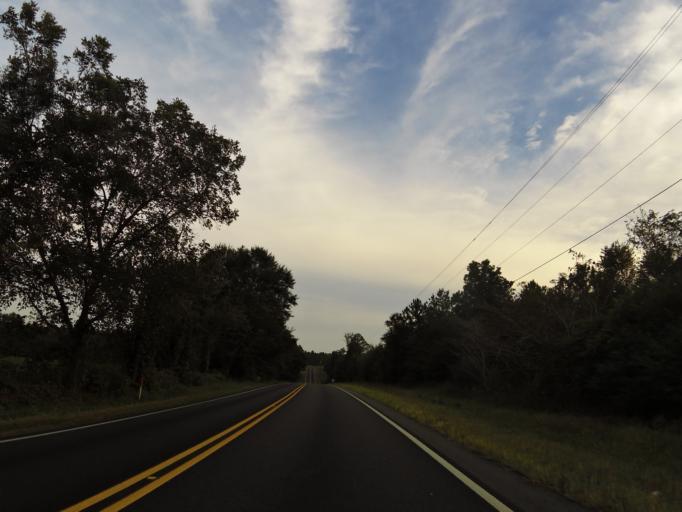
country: US
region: Alabama
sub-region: Escambia County
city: Atmore
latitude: 31.2010
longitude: -87.4676
